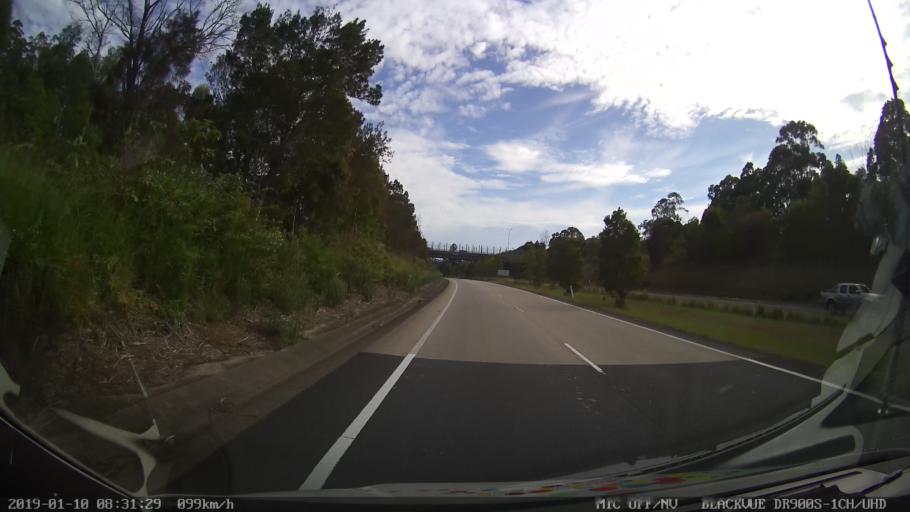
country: AU
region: New South Wales
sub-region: Coffs Harbour
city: Boambee
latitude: -30.3558
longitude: 153.0618
